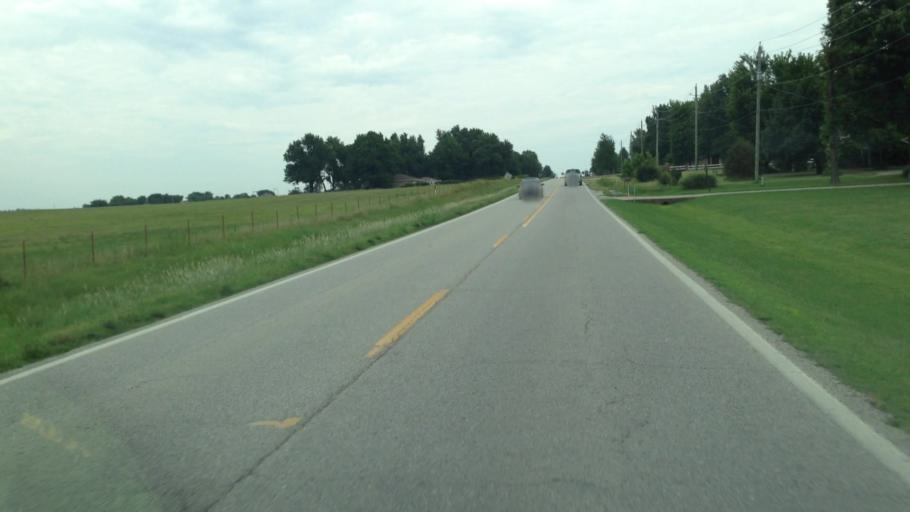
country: US
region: Oklahoma
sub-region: Craig County
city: Vinita
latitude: 36.6634
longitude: -95.1436
